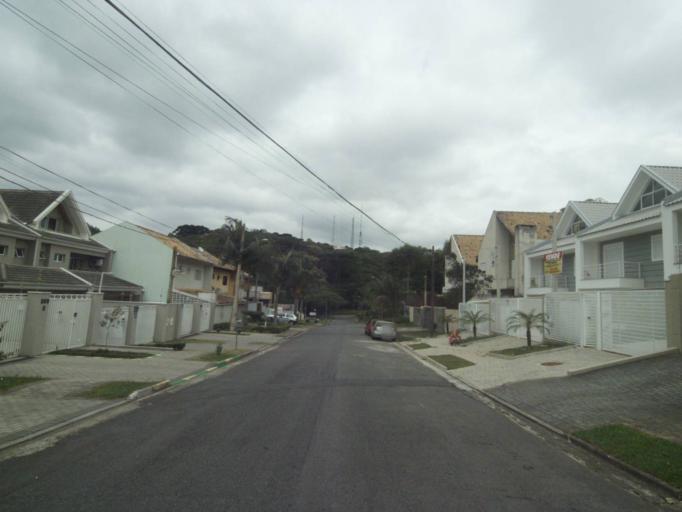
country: BR
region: Parana
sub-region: Curitiba
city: Curitiba
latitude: -25.3913
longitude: -49.2752
